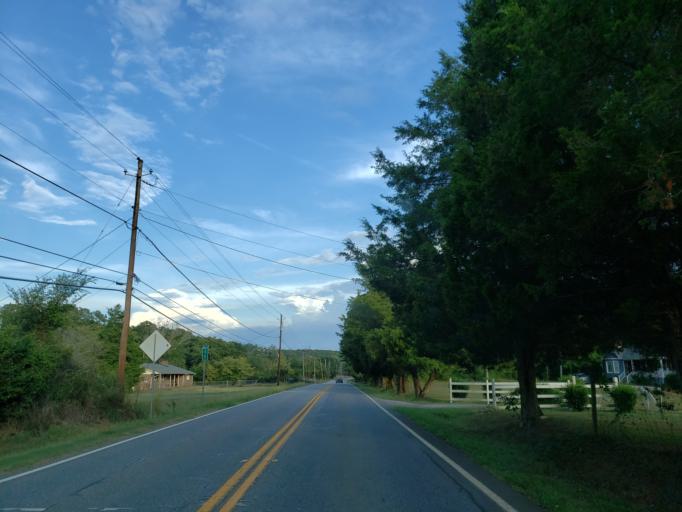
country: US
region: Georgia
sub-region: Bartow County
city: Cartersville
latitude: 34.2321
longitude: -84.8634
